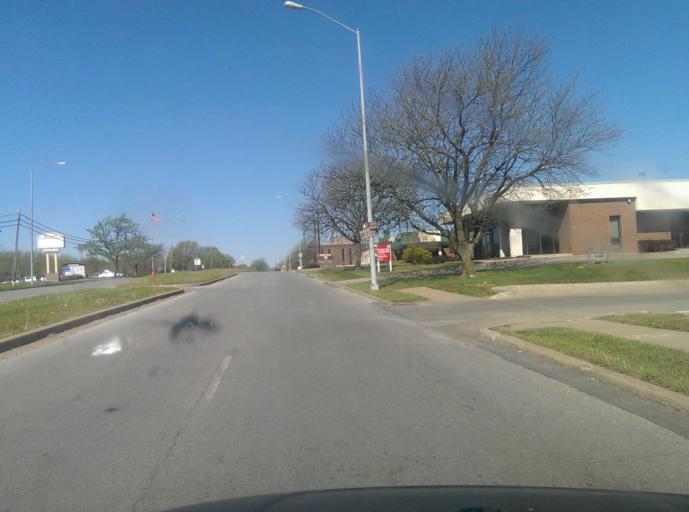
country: US
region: Kansas
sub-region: Johnson County
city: Leawood
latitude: 38.9259
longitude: -94.5837
